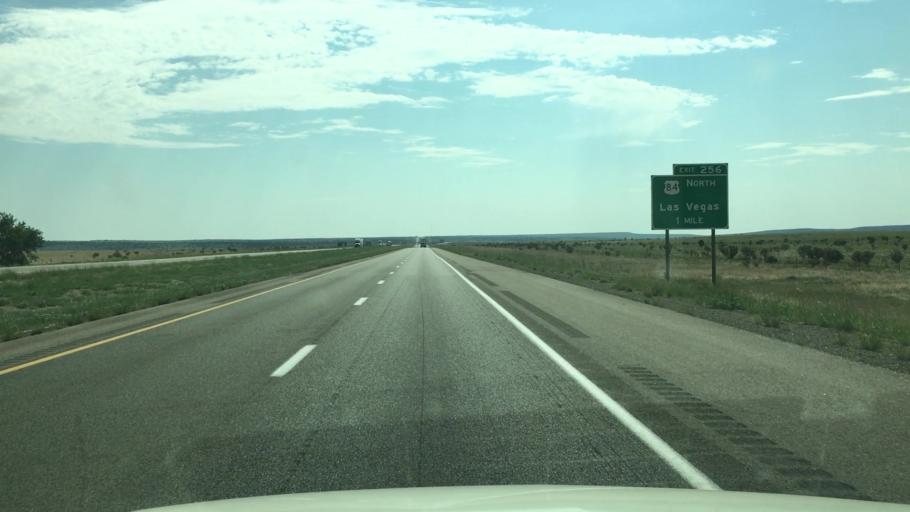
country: US
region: New Mexico
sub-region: Guadalupe County
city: Santa Rosa
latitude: 34.9774
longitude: -105.0125
